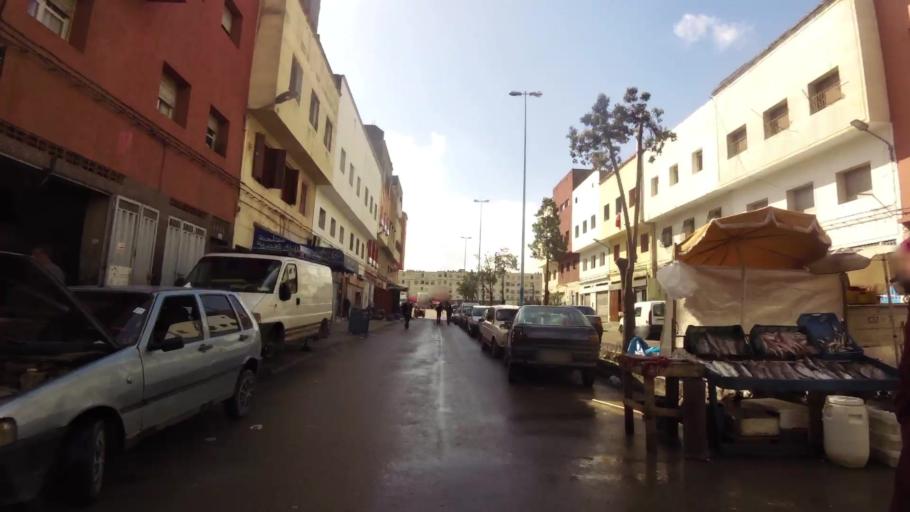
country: MA
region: Grand Casablanca
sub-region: Nouaceur
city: Bouskoura
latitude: 33.5286
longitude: -7.6729
